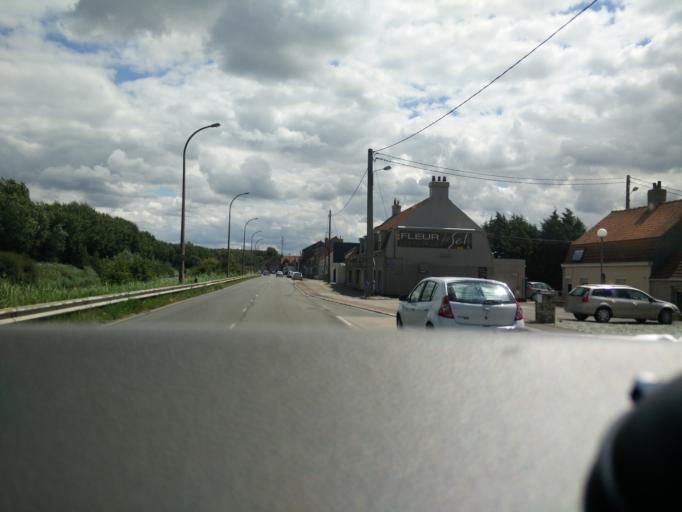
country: FR
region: Nord-Pas-de-Calais
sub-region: Departement du Nord
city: Coudekerque-Branche
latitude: 50.9997
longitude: 2.3876
